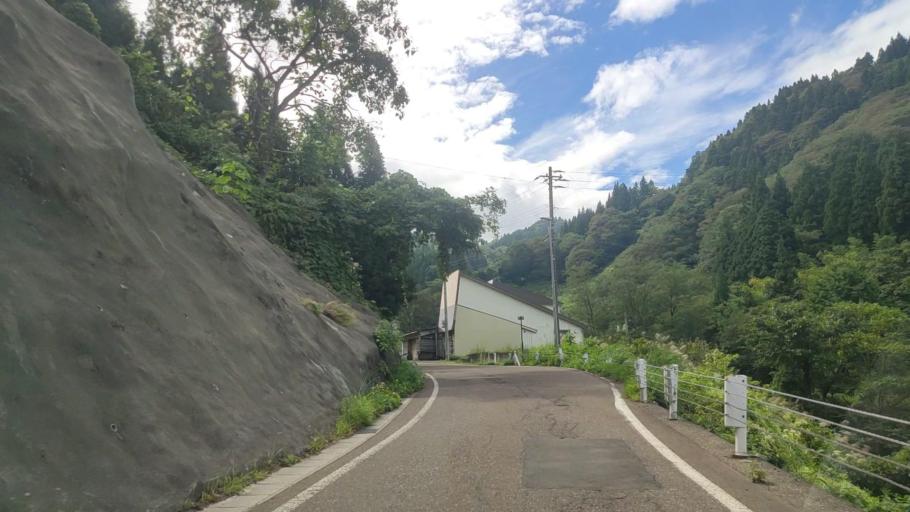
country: JP
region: Niigata
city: Arai
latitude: 36.9330
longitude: 138.2978
